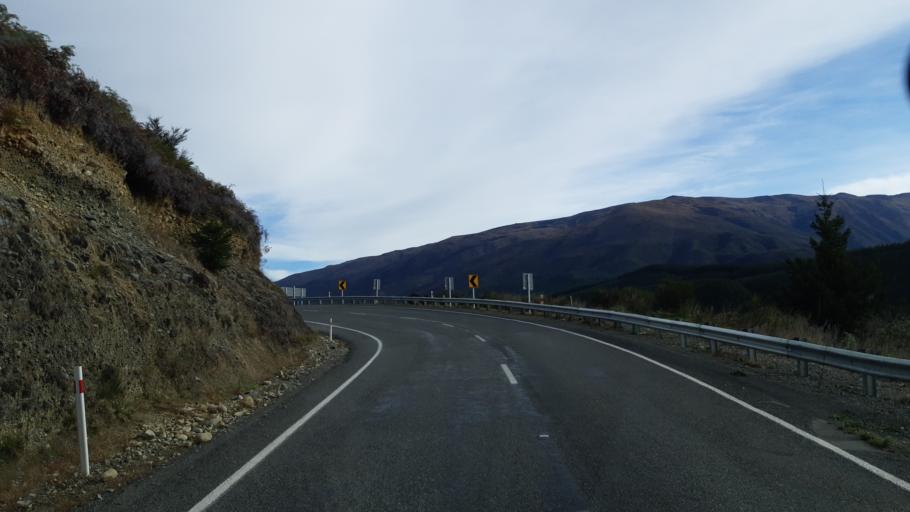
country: NZ
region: Tasman
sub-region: Tasman District
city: Wakefield
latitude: -41.6961
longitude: 173.1349
